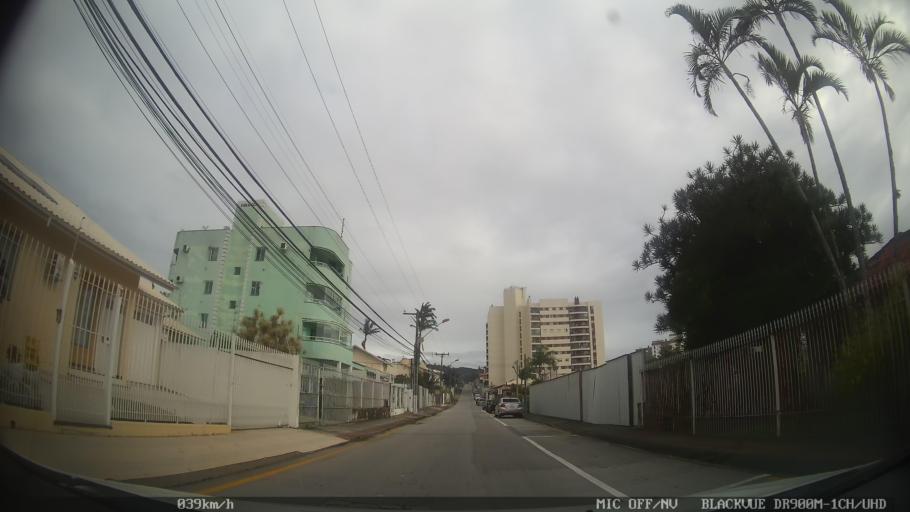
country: BR
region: Santa Catarina
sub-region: Sao Jose
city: Campinas
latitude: -27.5692
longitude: -48.6199
